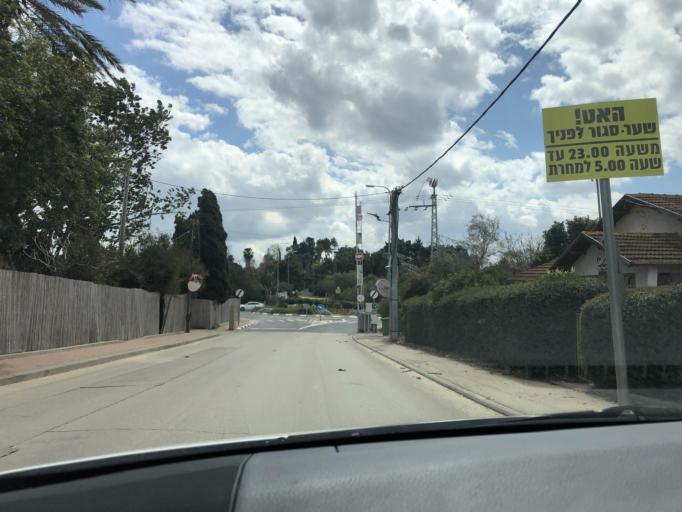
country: IL
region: Central District
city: Tel Mond
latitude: 32.2617
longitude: 34.9301
